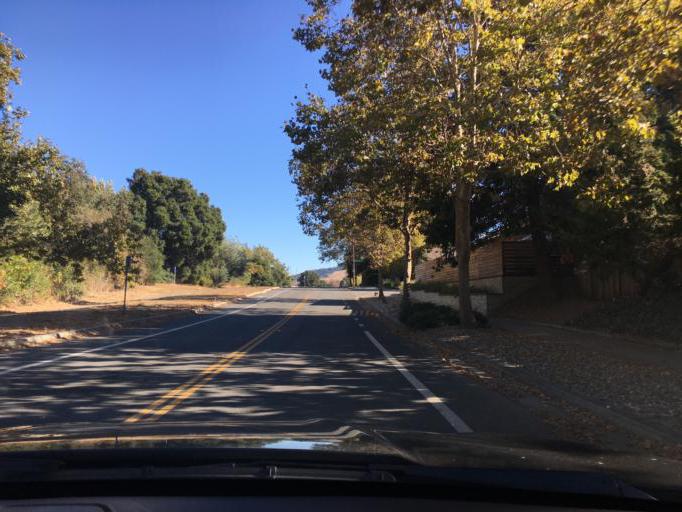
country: US
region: California
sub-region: Santa Clara County
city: Seven Trees
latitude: 37.2087
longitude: -121.8257
